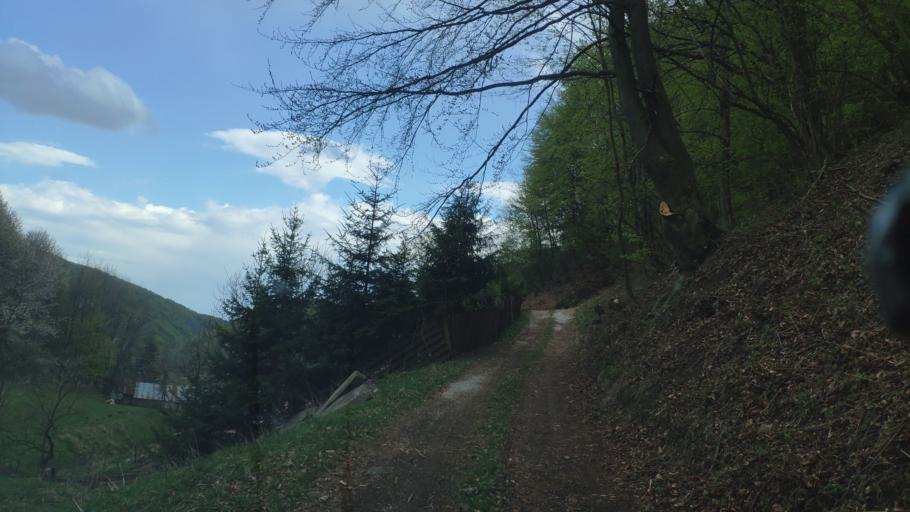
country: SK
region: Kosicky
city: Medzev
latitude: 48.6699
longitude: 20.8331
